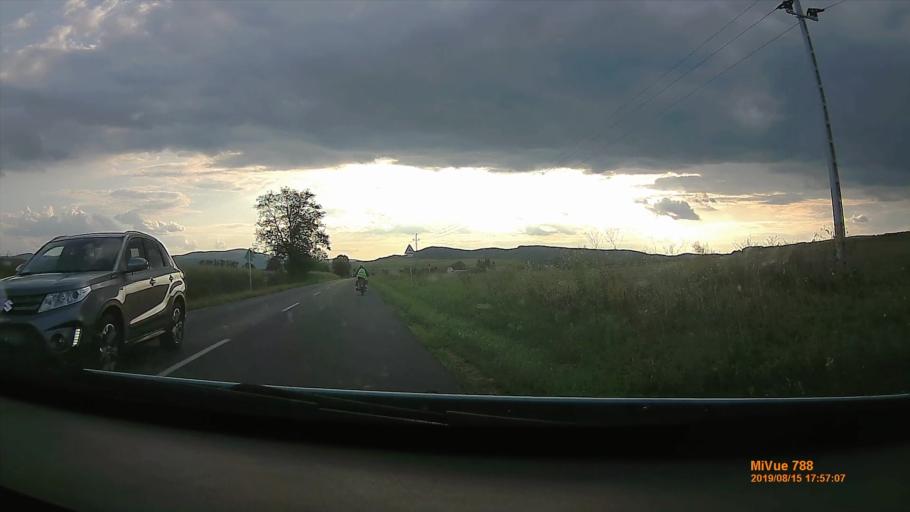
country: HU
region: Borsod-Abauj-Zemplen
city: Sajoszentpeter
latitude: 48.1866
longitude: 20.6633
